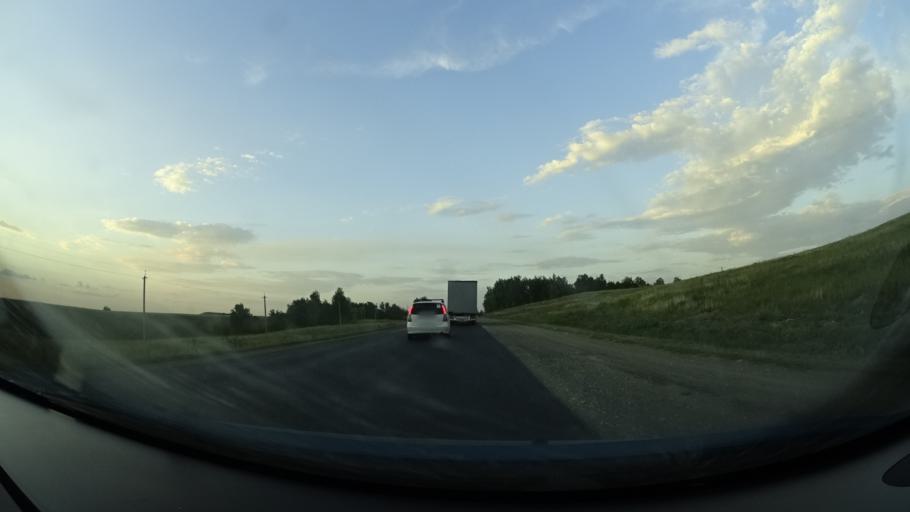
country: RU
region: Orenburg
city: Severnoye
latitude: 54.1478
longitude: 52.6133
